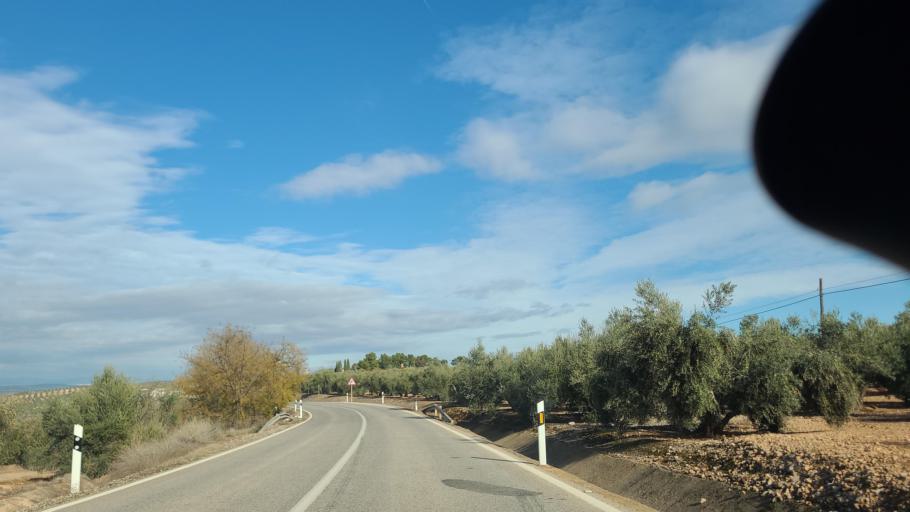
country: ES
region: Andalusia
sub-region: Provincia de Jaen
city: Espeluy
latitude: 38.0289
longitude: -3.8665
